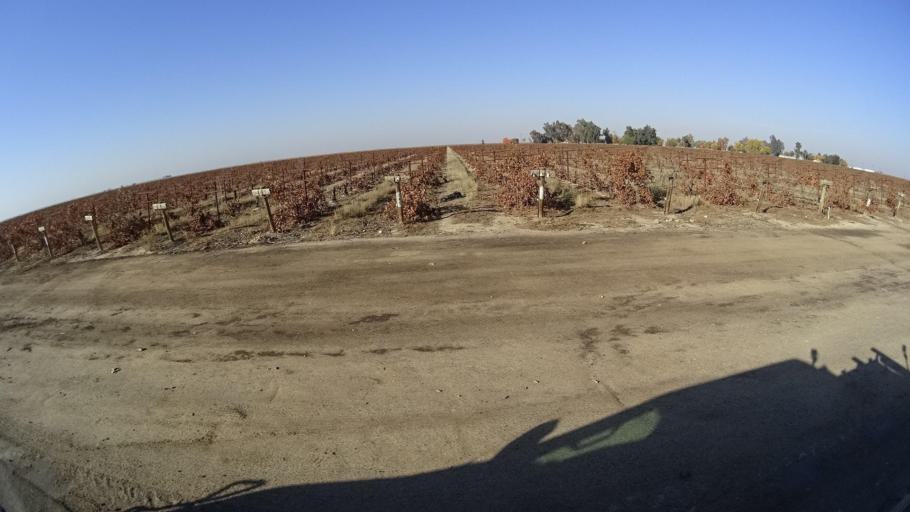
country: US
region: California
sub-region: Kern County
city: Delano
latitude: 35.7426
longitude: -119.1697
